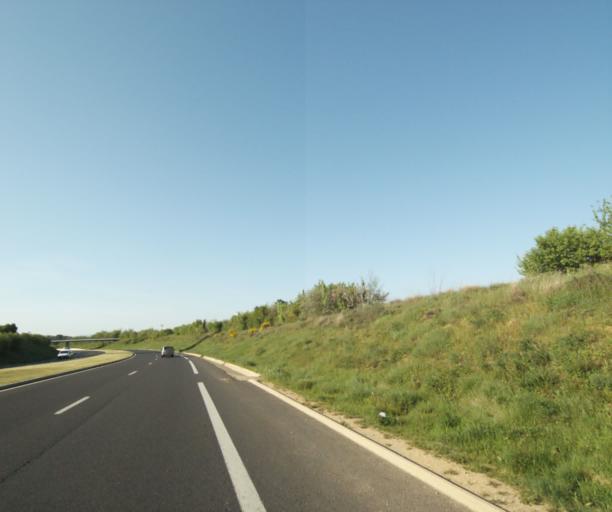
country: FR
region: Languedoc-Roussillon
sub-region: Departement de l'Herault
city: Le Cres
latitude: 43.6325
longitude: 3.9355
